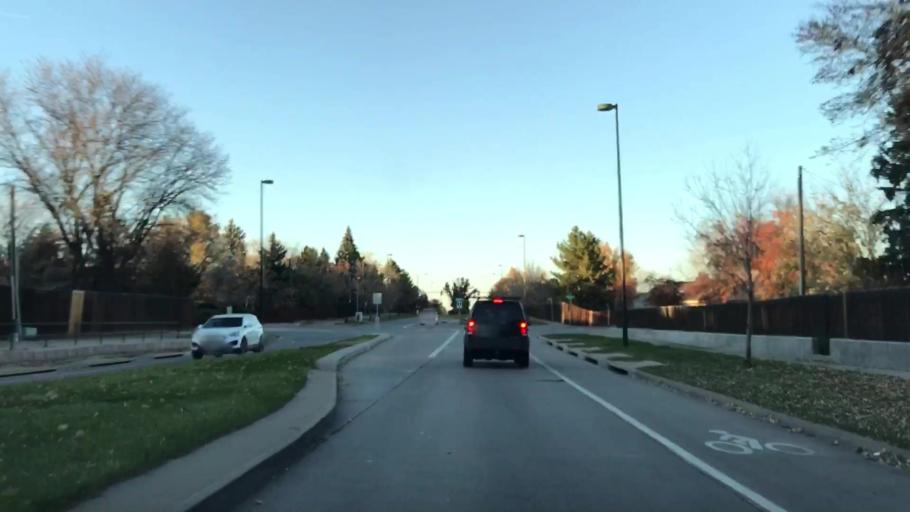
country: US
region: Colorado
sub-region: Arapahoe County
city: Glendale
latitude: 39.6565
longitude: -104.8847
